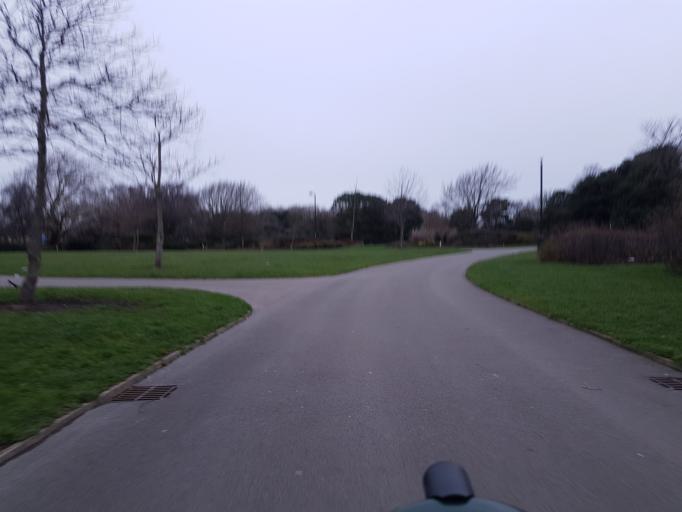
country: GB
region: England
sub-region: Liverpool
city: Liverpool
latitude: 53.4348
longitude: -2.9672
